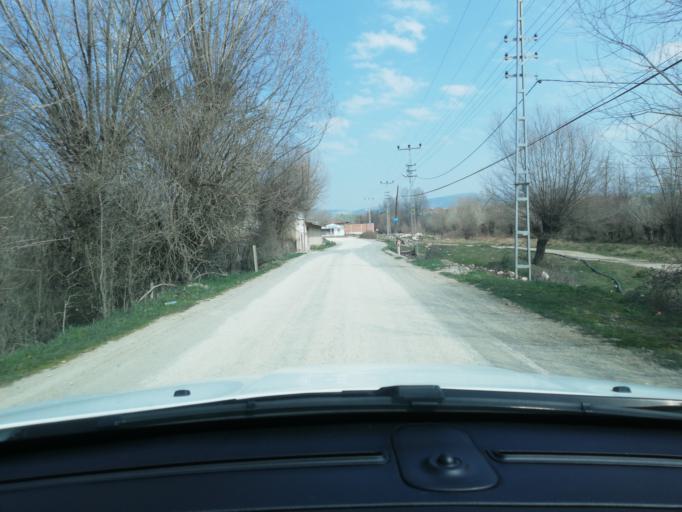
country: TR
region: Kastamonu
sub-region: Cide
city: Kastamonu
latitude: 41.4545
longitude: 33.7673
